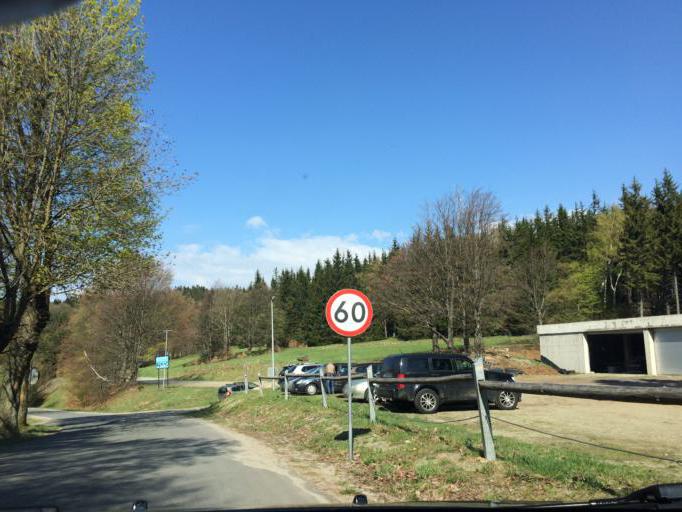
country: PL
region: Lower Silesian Voivodeship
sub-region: Powiat klodzki
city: Jugow
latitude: 50.6554
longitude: 16.5263
